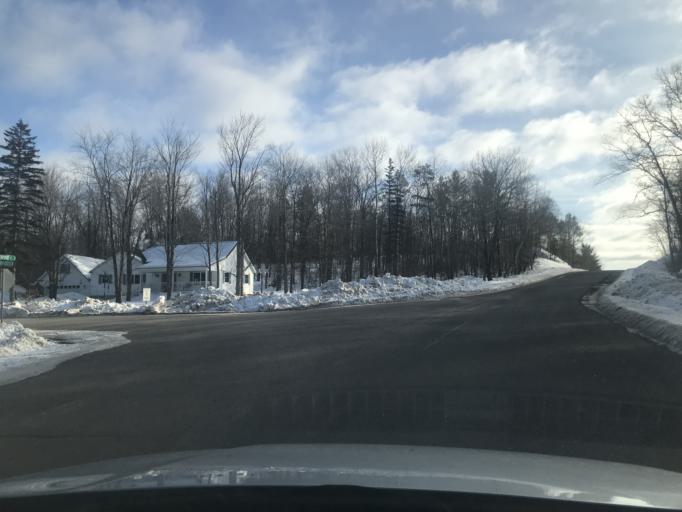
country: US
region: Wisconsin
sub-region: Marinette County
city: Niagara
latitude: 45.6261
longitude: -87.9676
